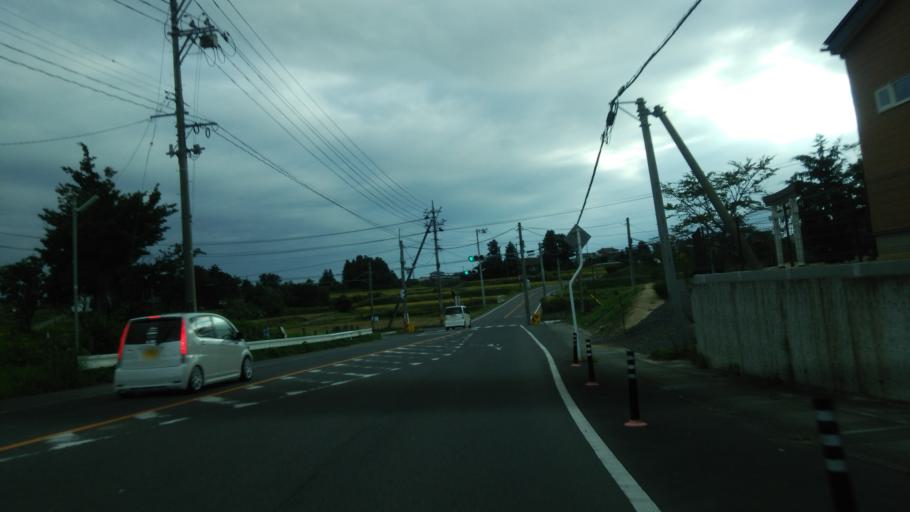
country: JP
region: Fukushima
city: Koriyama
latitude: 37.3508
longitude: 140.3398
